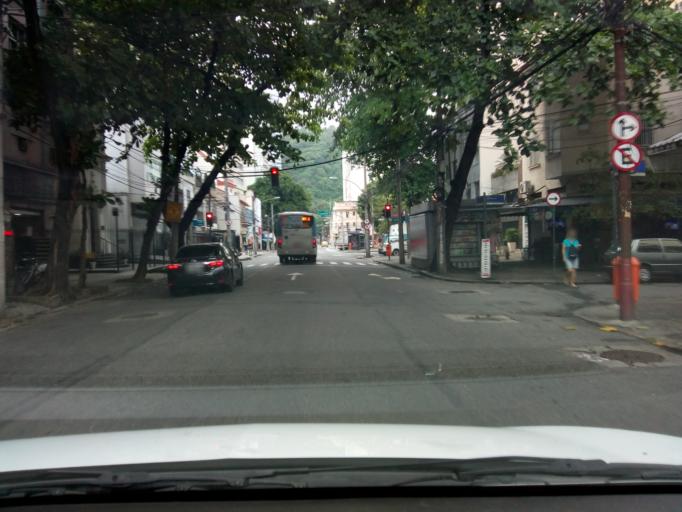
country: BR
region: Rio de Janeiro
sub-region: Rio De Janeiro
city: Rio de Janeiro
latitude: -22.9529
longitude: -43.1820
